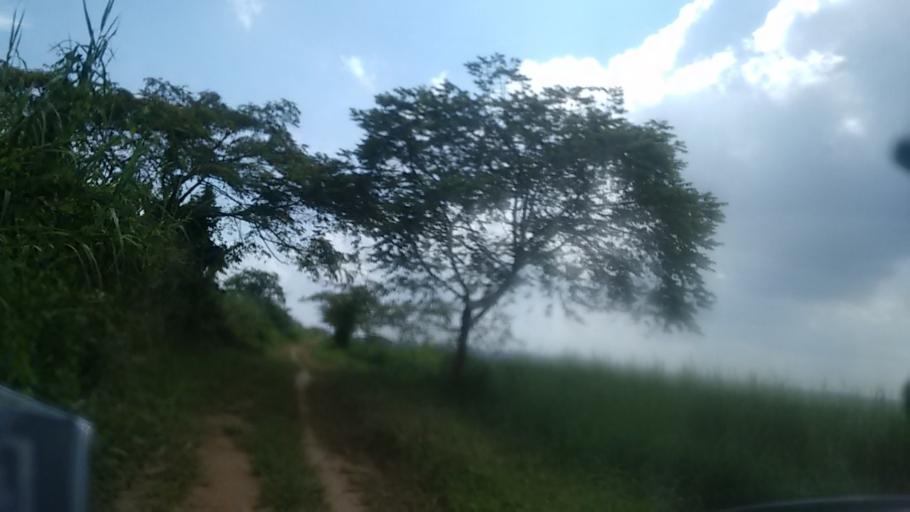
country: IN
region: Kerala
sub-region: Thrissur District
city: Trichur
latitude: 10.5305
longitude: 76.1476
